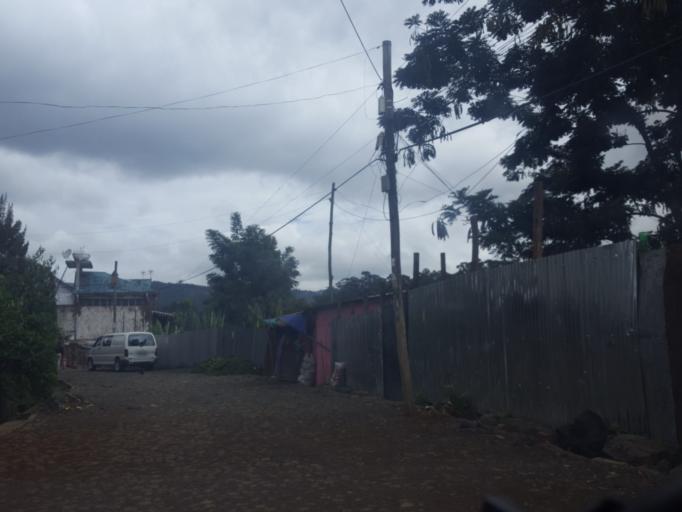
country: ET
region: Adis Abeba
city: Addis Ababa
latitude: 9.0547
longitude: 38.7662
